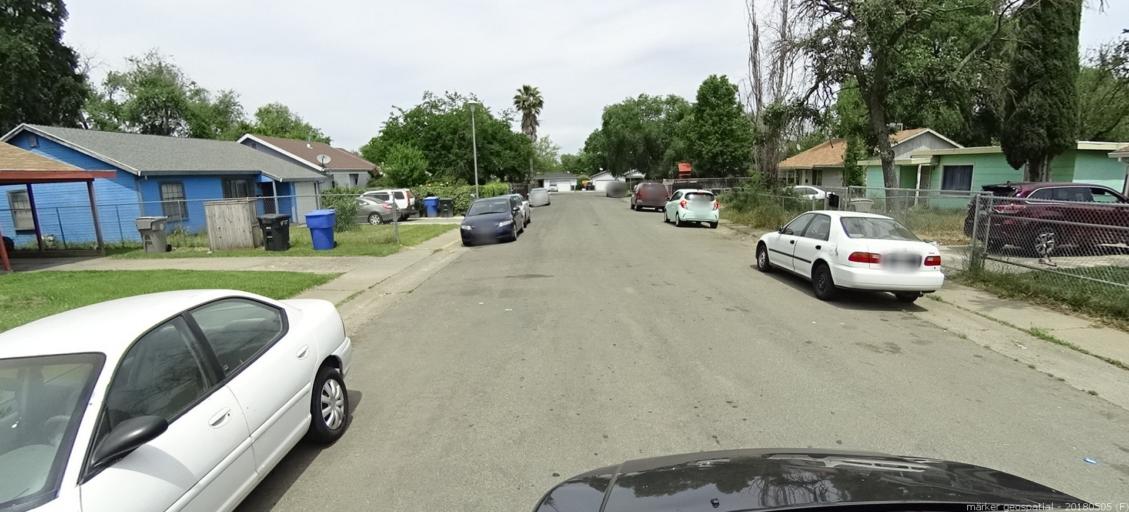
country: US
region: California
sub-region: Sacramento County
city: Rio Linda
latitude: 38.6392
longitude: -121.4351
